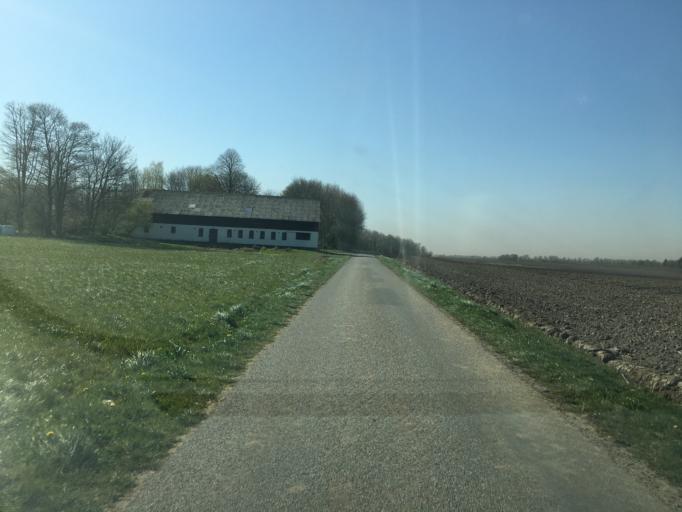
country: DK
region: South Denmark
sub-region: Aabenraa Kommune
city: Rodekro
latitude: 55.1102
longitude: 9.2033
